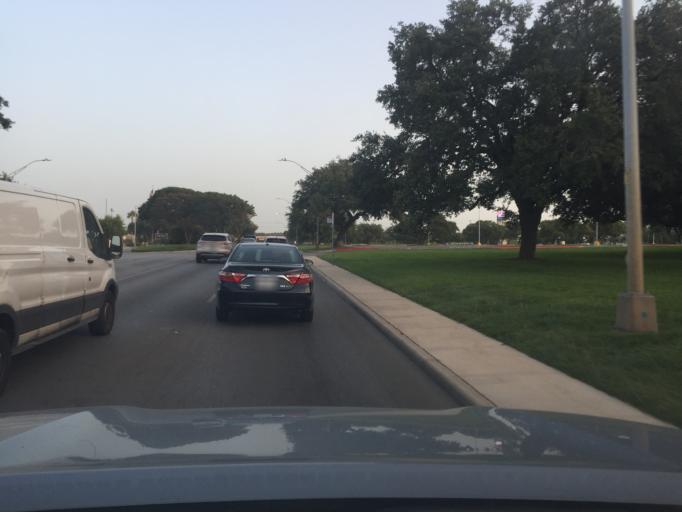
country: US
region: Texas
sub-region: Bexar County
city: Hollywood Park
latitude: 29.6123
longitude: -98.4934
